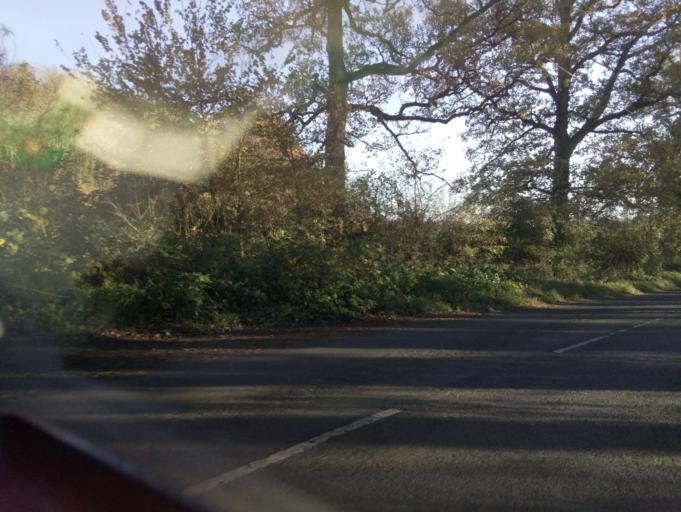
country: GB
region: England
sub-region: Somerset
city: Milborne Port
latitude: 50.9858
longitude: -2.4636
